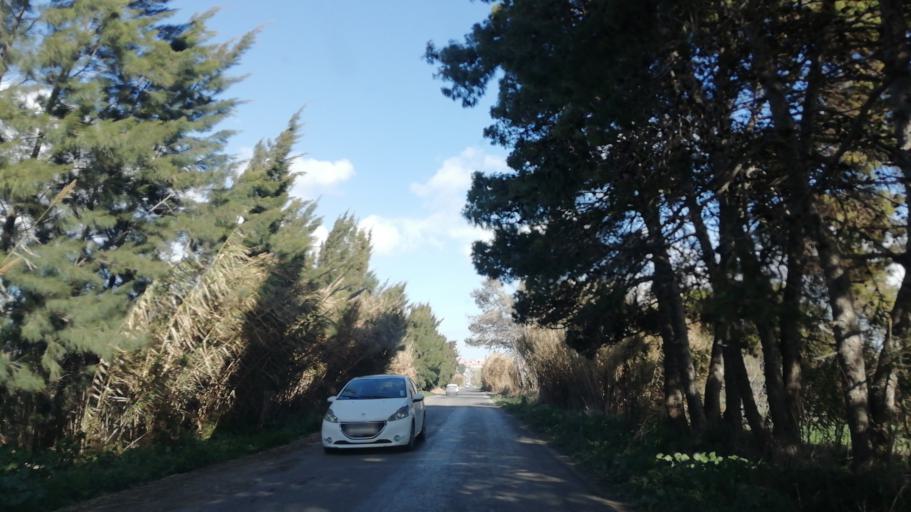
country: DZ
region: Oran
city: Es Senia
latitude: 35.6216
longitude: -0.6615
